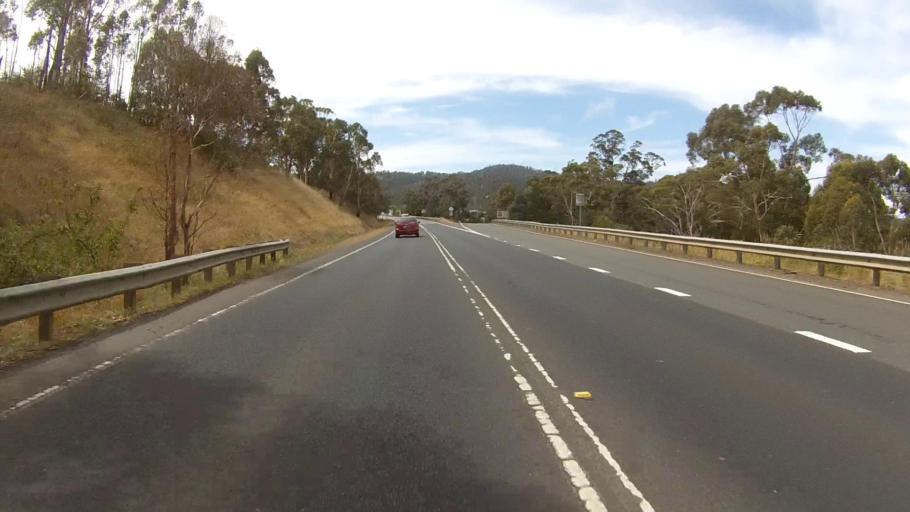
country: AU
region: Tasmania
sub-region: Kingborough
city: Kingston
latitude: -42.9723
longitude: 147.3072
